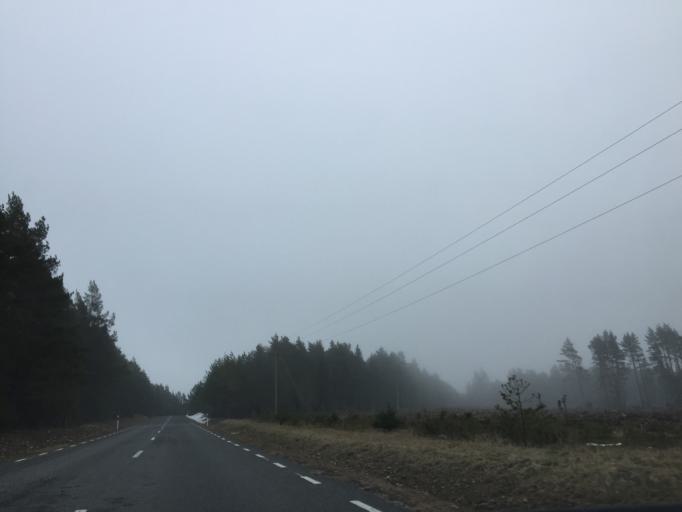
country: EE
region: Saare
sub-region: Kuressaare linn
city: Kuressaare
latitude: 58.4662
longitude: 22.0413
